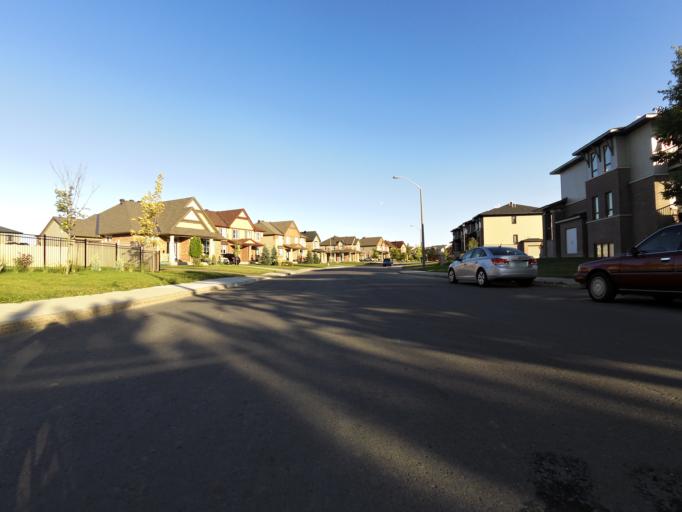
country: CA
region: Ontario
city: Bells Corners
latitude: 45.2872
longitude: -75.7320
